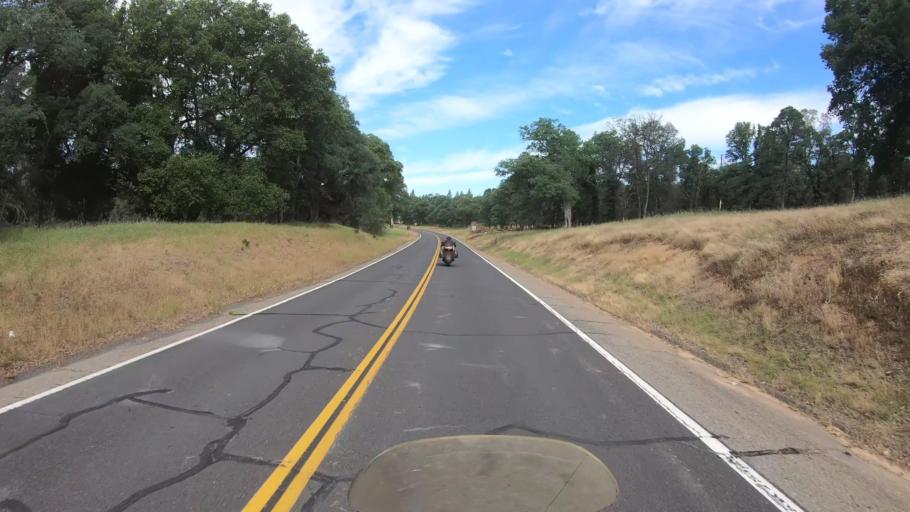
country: US
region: California
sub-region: Tuolumne County
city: Tuolumne City
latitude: 37.8577
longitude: -120.1754
